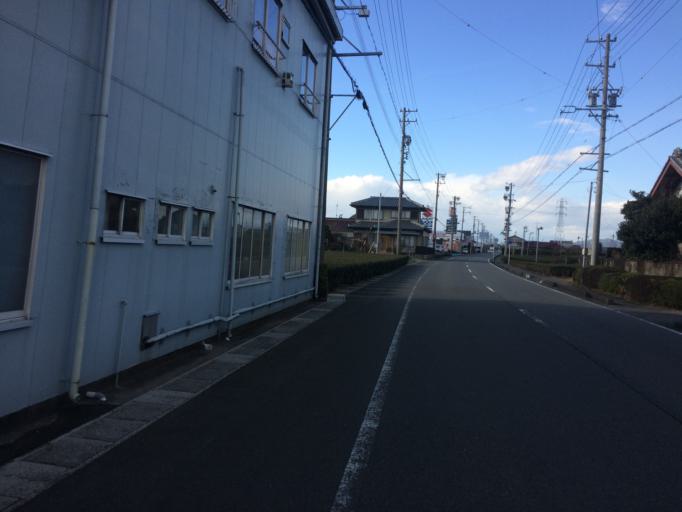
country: JP
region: Shizuoka
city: Kanaya
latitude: 34.7967
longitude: 138.1372
